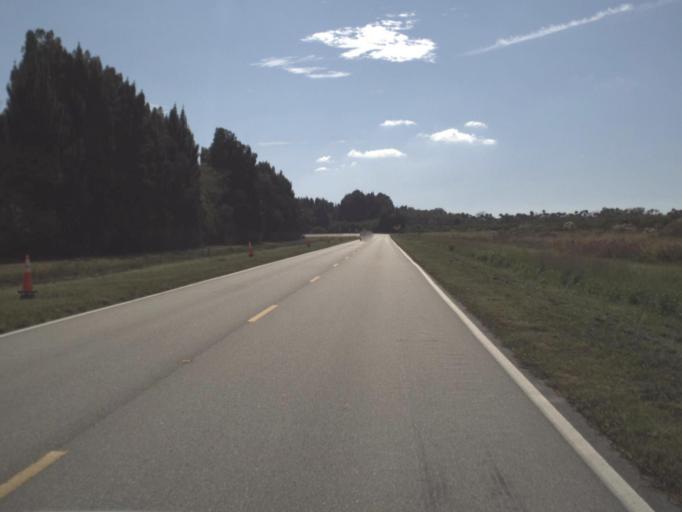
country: US
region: Florida
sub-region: Brevard County
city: Merritt Island
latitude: 28.5063
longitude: -80.6756
